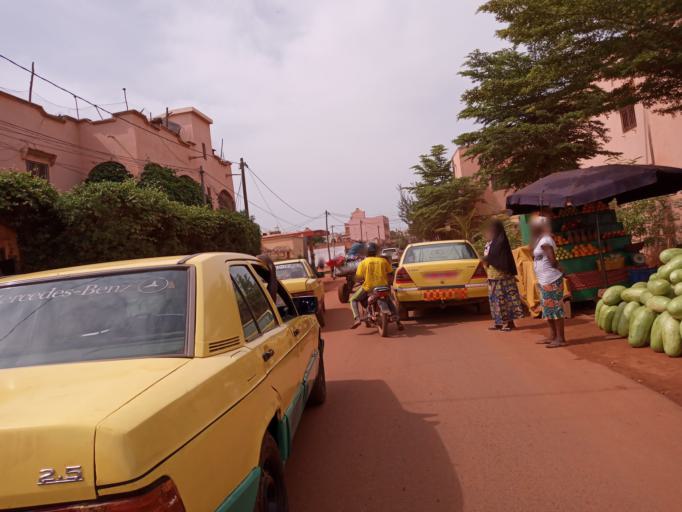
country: ML
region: Bamako
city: Bamako
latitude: 12.5610
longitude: -7.9902
